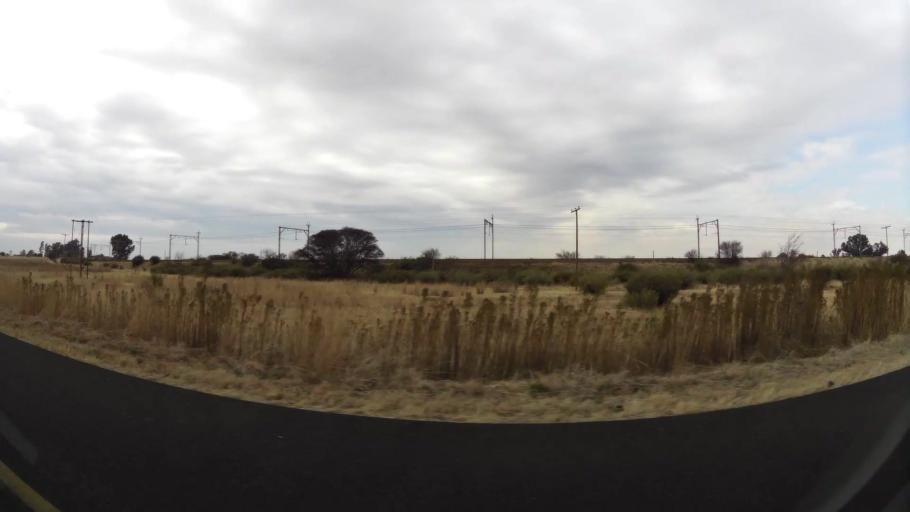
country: ZA
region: Orange Free State
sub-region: Fezile Dabi District Municipality
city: Kroonstad
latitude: -27.6327
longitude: 27.2501
